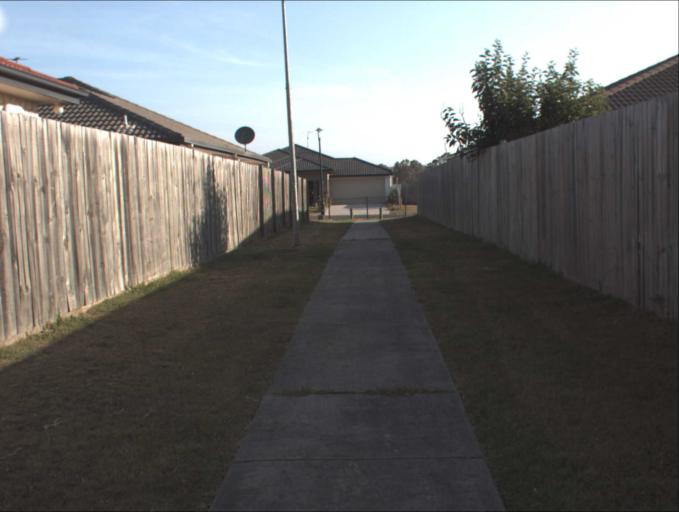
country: AU
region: Queensland
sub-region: Logan
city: Beenleigh
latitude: -27.6850
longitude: 153.1743
